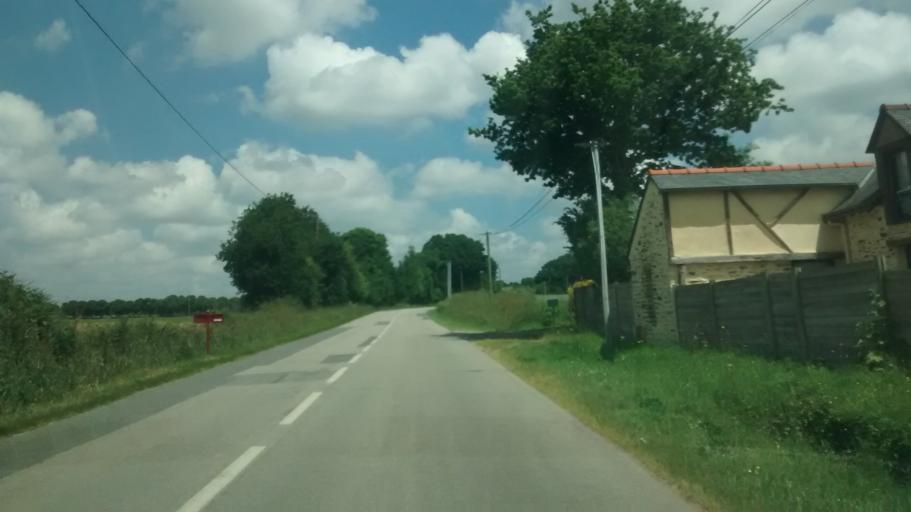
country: FR
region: Brittany
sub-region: Departement du Morbihan
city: Malestroit
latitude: 47.8225
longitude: -2.3602
